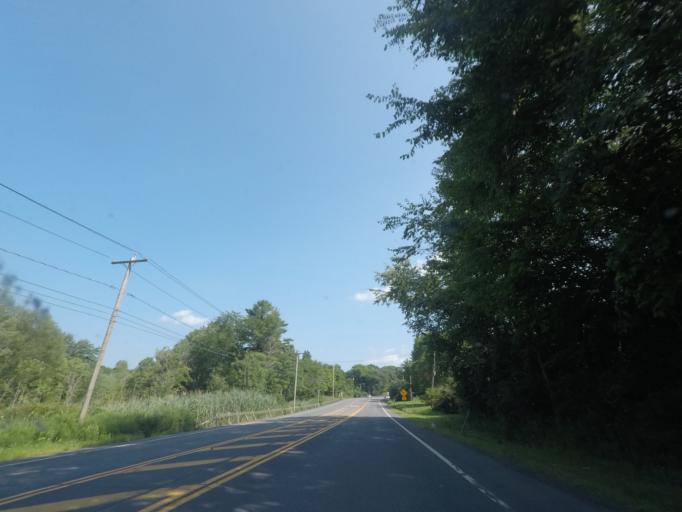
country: US
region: New York
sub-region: Rensselaer County
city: East Greenbush
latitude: 42.5462
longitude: -73.6686
